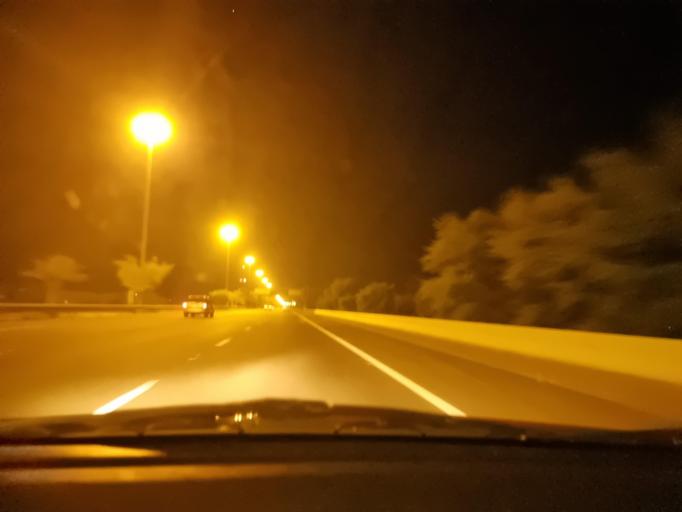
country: AE
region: Abu Dhabi
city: Al Ain
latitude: 24.1968
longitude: 55.3624
